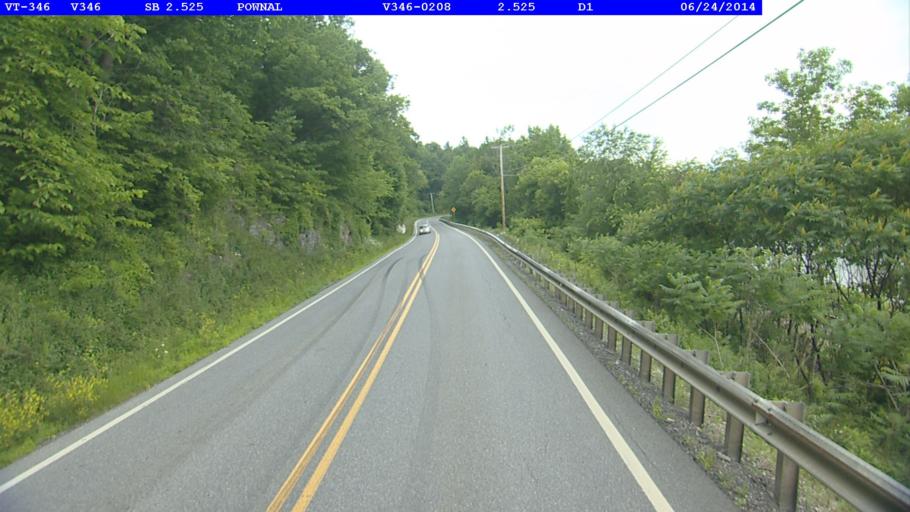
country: US
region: Massachusetts
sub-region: Berkshire County
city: Williamstown
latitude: 42.7931
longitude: -73.2575
